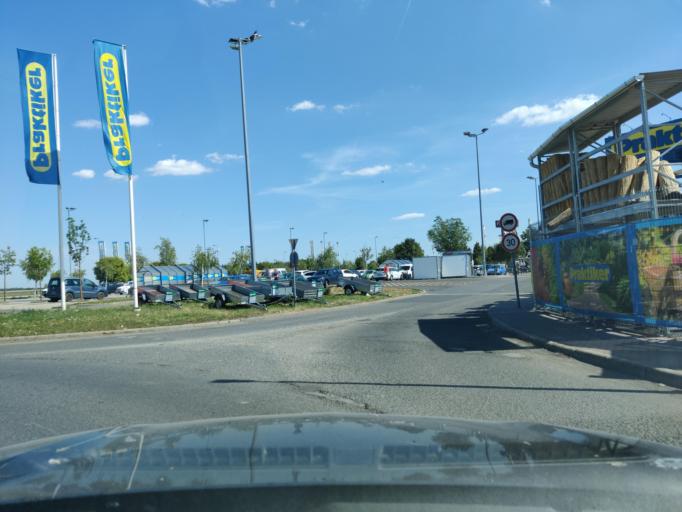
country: HU
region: Vas
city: Szombathely
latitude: 47.2382
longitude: 16.6540
